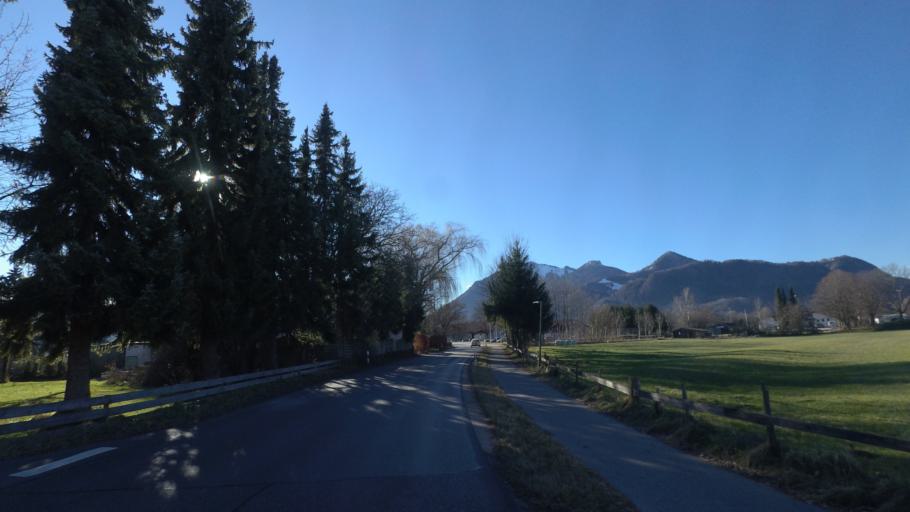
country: DE
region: Bavaria
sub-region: Upper Bavaria
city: Grassau
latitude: 47.7847
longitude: 12.4654
